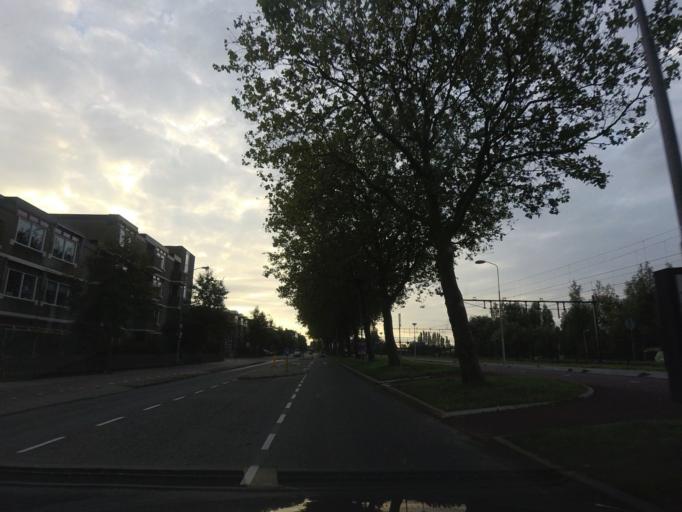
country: NL
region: North Holland
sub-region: Gemeente Zaanstad
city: Zaanstad
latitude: 52.4888
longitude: 4.7955
